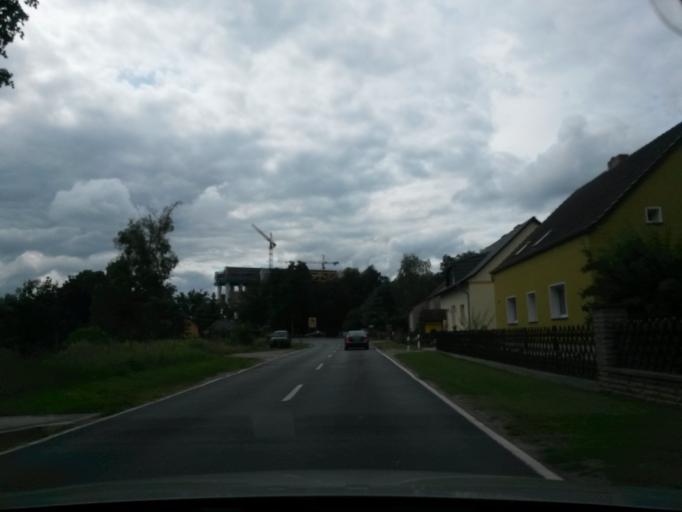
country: DE
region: Brandenburg
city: Liepe
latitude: 52.8539
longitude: 13.9458
